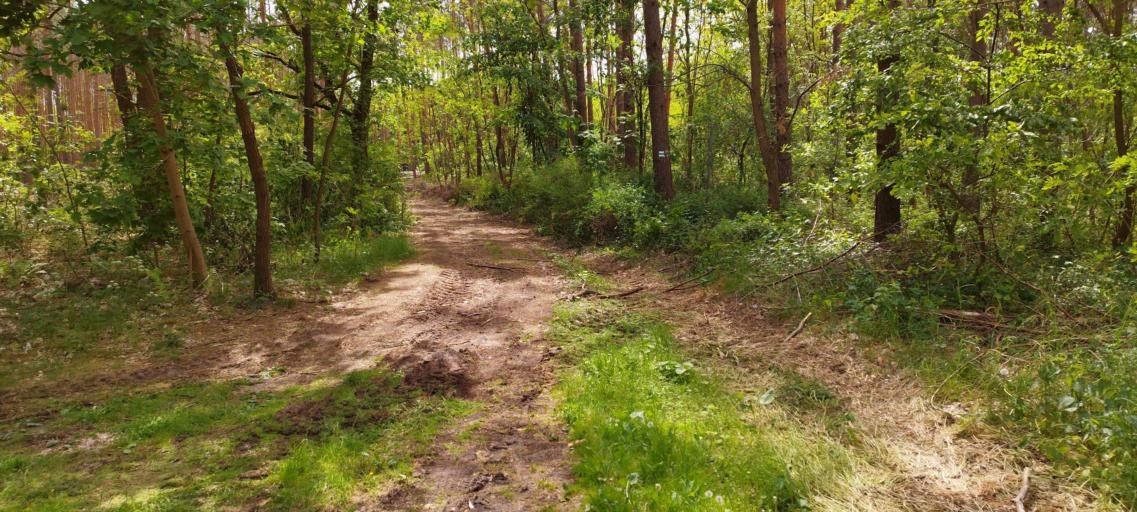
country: DE
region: Brandenburg
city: Rauen
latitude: 52.3367
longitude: 14.0147
